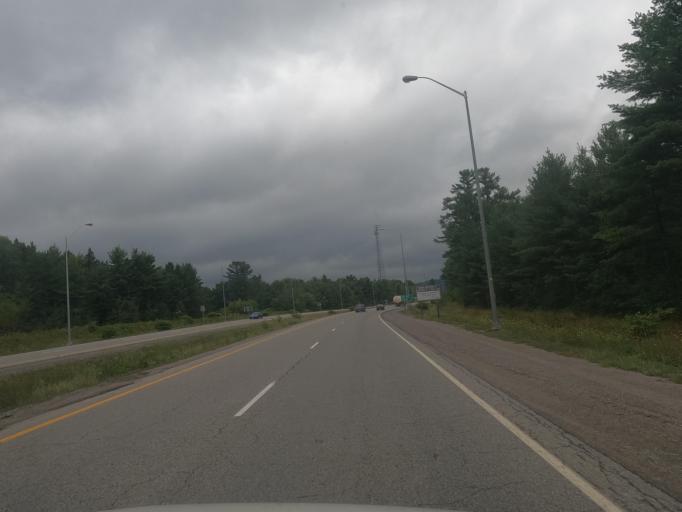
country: CA
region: Ontario
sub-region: Algoma
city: Sault Ste. Marie
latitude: 46.5427
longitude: -84.2307
